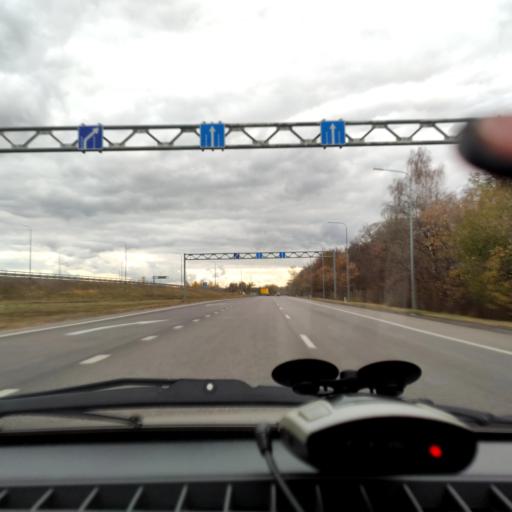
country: RU
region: Voronezj
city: Podgornoye
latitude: 51.8370
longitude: 39.2138
